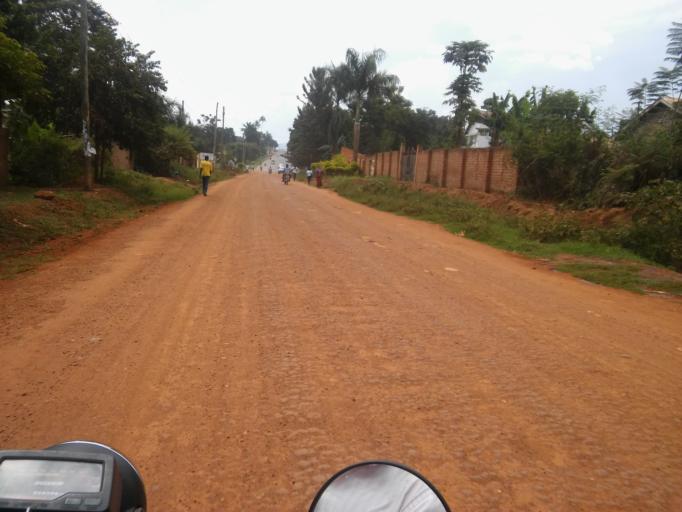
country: UG
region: Eastern Region
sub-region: Mbale District
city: Mbale
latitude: 1.0729
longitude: 34.1697
